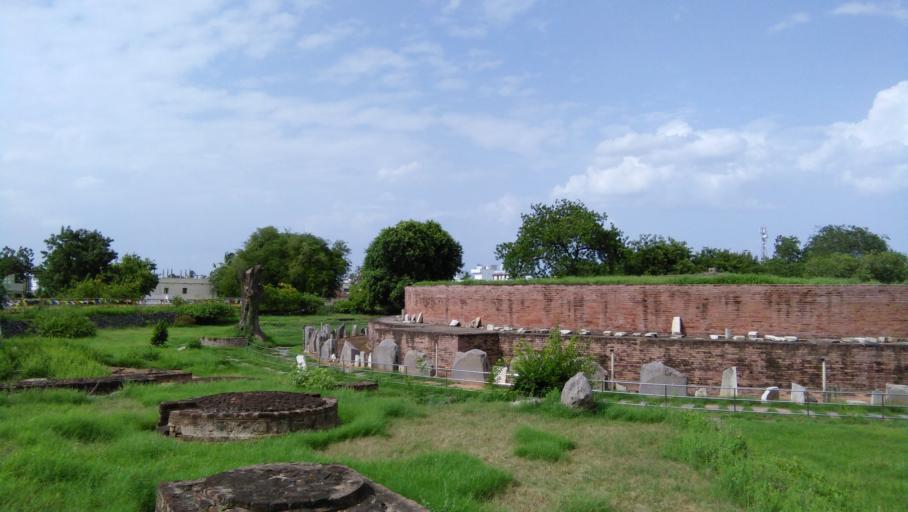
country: IN
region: Andhra Pradesh
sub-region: Krishna
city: Kondapalle
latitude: 16.5755
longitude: 80.3561
